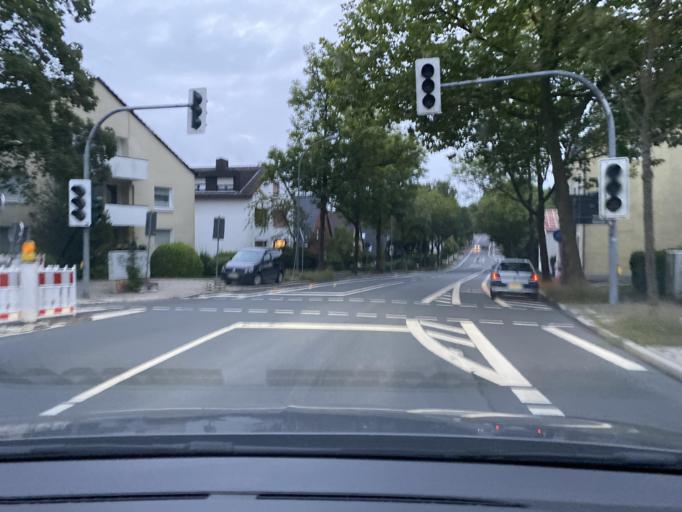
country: DE
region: North Rhine-Westphalia
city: Hattingen
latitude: 51.4411
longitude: 7.1950
